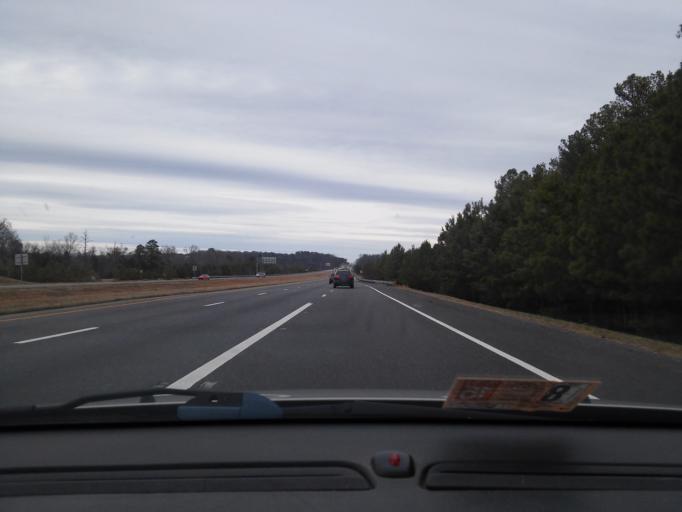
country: US
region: Virginia
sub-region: Henrico County
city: Short Pump
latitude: 37.5628
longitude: -77.6870
